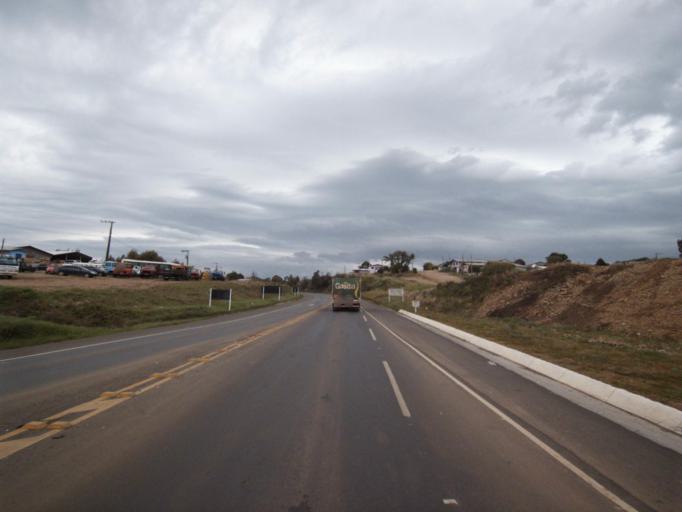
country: BR
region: Santa Catarina
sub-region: Concordia
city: Concordia
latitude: -27.0255
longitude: -51.8855
